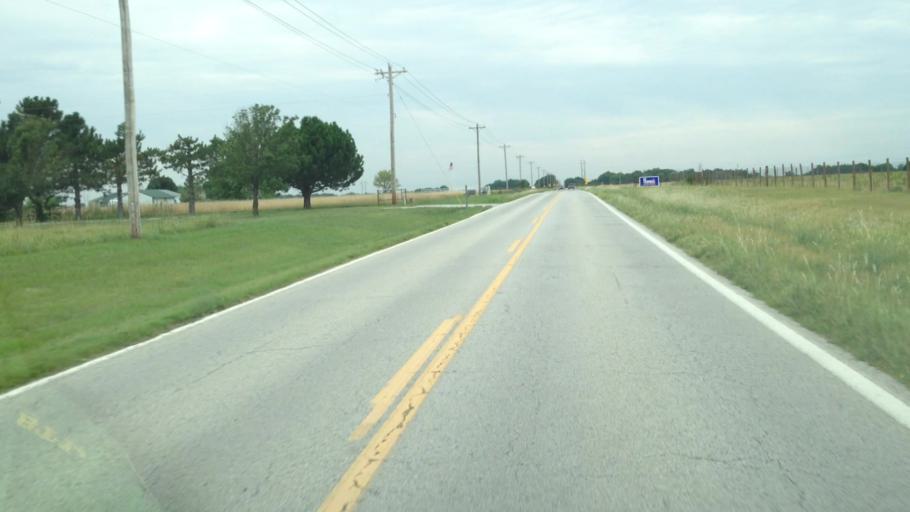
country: US
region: Oklahoma
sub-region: Delaware County
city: Cleora
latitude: 36.6125
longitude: -94.9753
